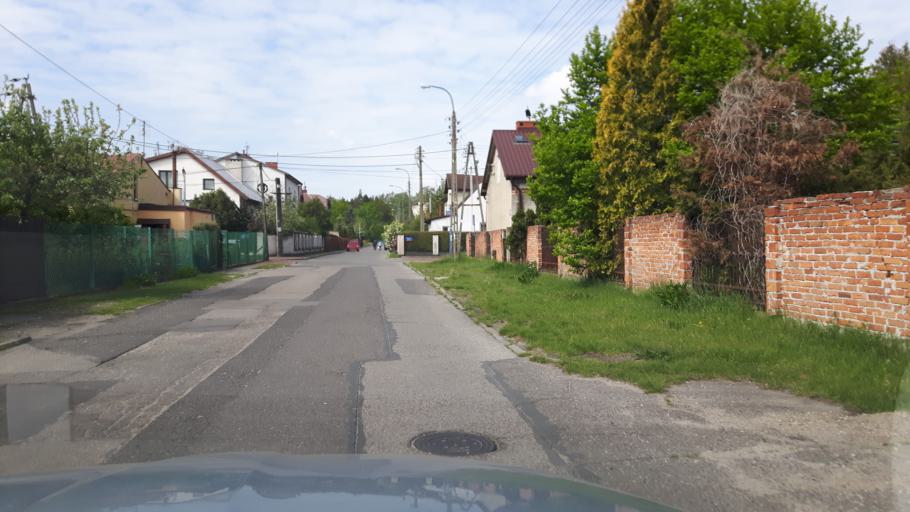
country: PL
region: Masovian Voivodeship
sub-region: Warszawa
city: Rembertow
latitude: 52.2490
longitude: 21.1877
